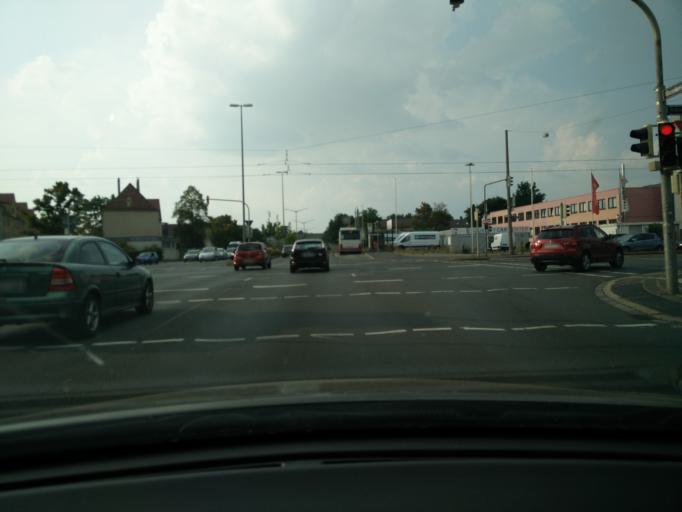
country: DE
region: Bavaria
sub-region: Regierungsbezirk Mittelfranken
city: Nuernberg
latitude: 49.4555
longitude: 11.1187
